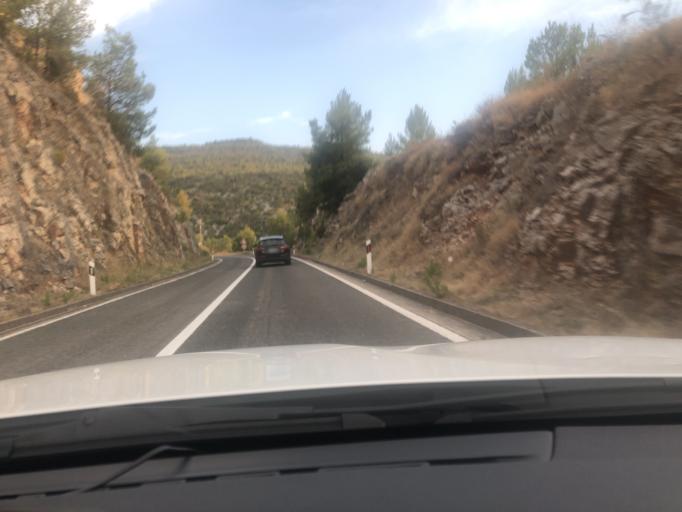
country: HR
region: Splitsko-Dalmatinska
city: Stari Grad
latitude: 43.1703
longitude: 16.5634
